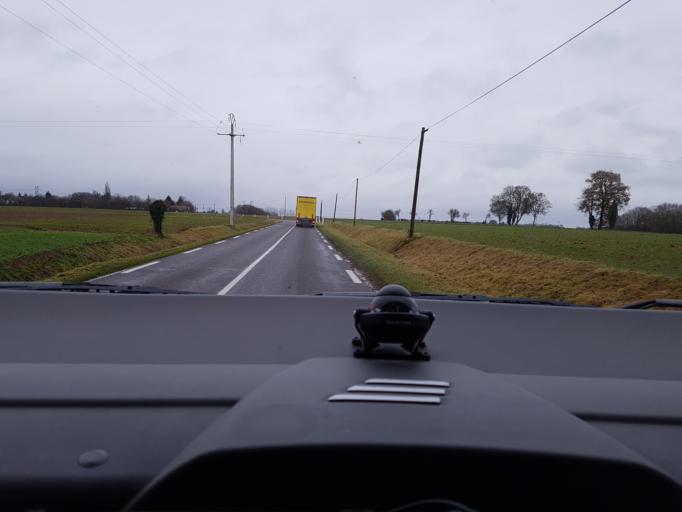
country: FR
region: Haute-Normandie
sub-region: Departement de la Seine-Maritime
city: Gournay-en-Bray
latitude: 49.4410
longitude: 1.6585
